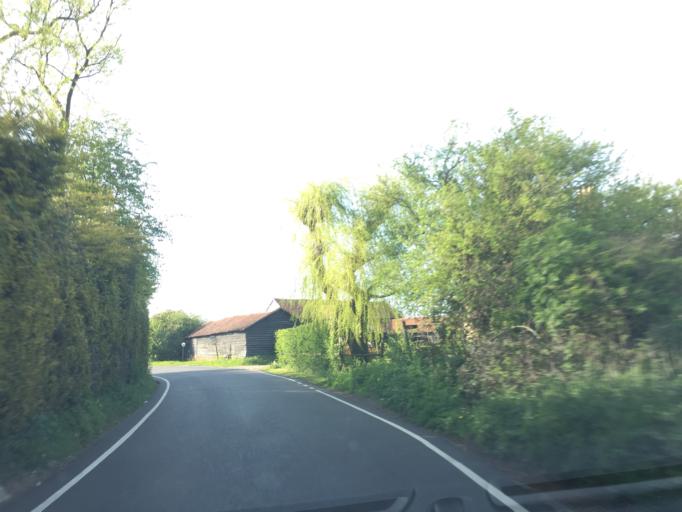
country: GB
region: England
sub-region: Essex
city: Epping
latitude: 51.7345
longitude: 0.1135
